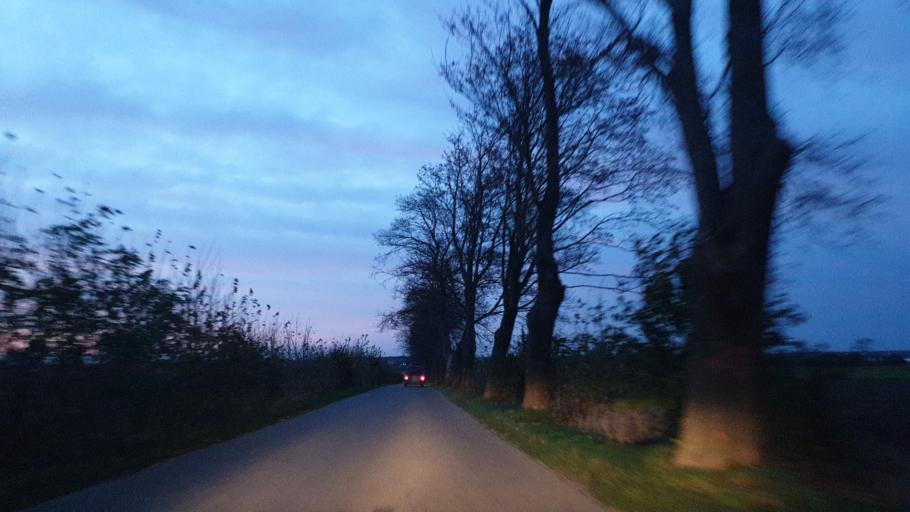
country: PL
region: Pomeranian Voivodeship
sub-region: Powiat pucki
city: Krokowa
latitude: 54.7797
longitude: 18.2037
